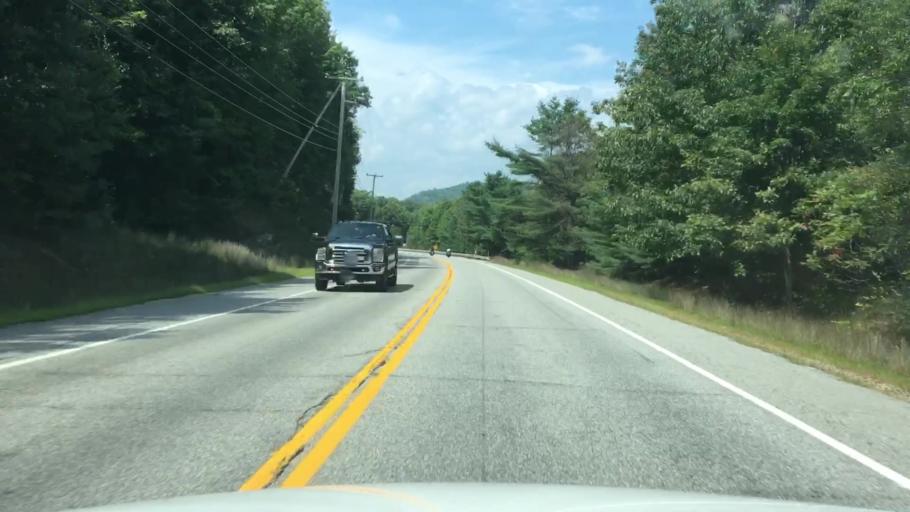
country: US
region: Maine
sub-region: Oxford County
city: Peru
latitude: 44.5037
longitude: -70.4016
